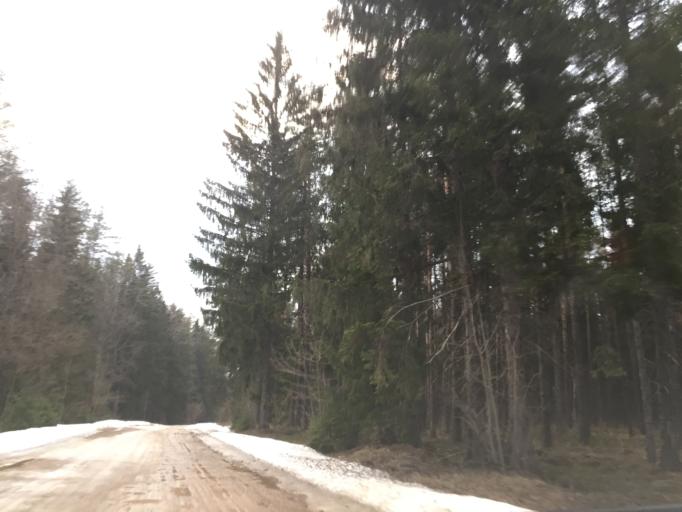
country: LV
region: Vecpiebalga
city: Vecpiebalga
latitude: 57.1343
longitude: 25.6381
